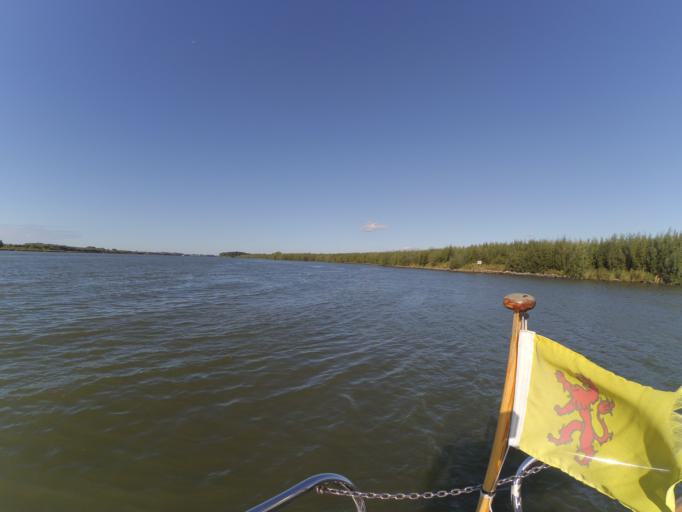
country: NL
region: South Holland
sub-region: Gemeente Binnenmaas
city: Heinenoord
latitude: 51.8369
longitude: 4.4932
